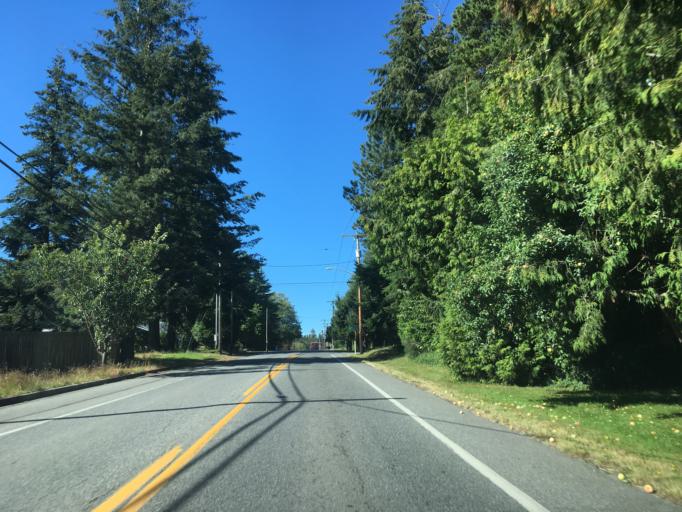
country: US
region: Washington
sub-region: Skagit County
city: Sedro-Woolley
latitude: 48.5226
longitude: -122.2259
